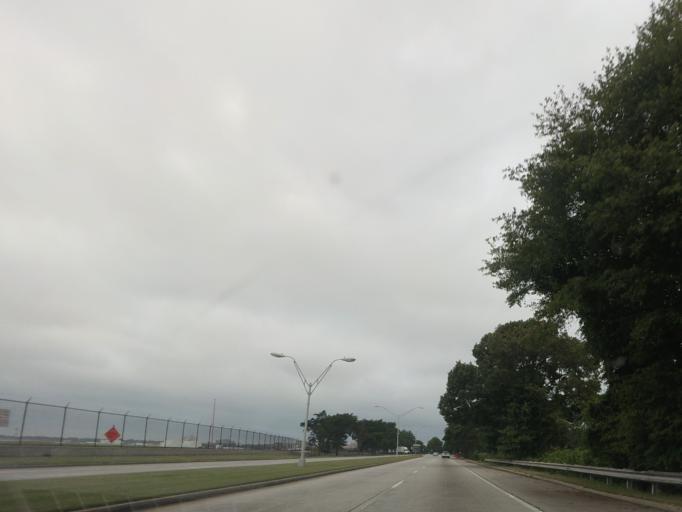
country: US
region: Georgia
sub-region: Fulton County
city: Hapeville
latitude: 33.6511
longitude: -84.4065
